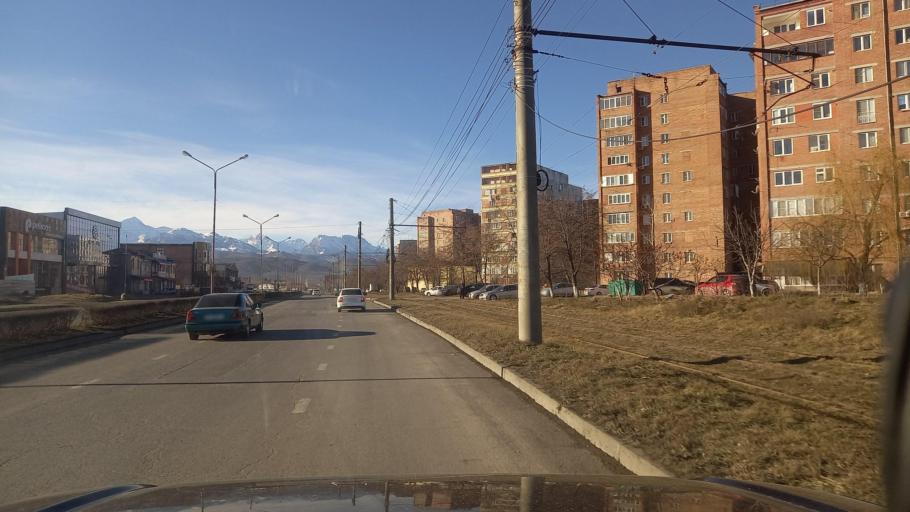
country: RU
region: North Ossetia
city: Vladikavkaz
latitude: 43.0388
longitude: 44.6446
